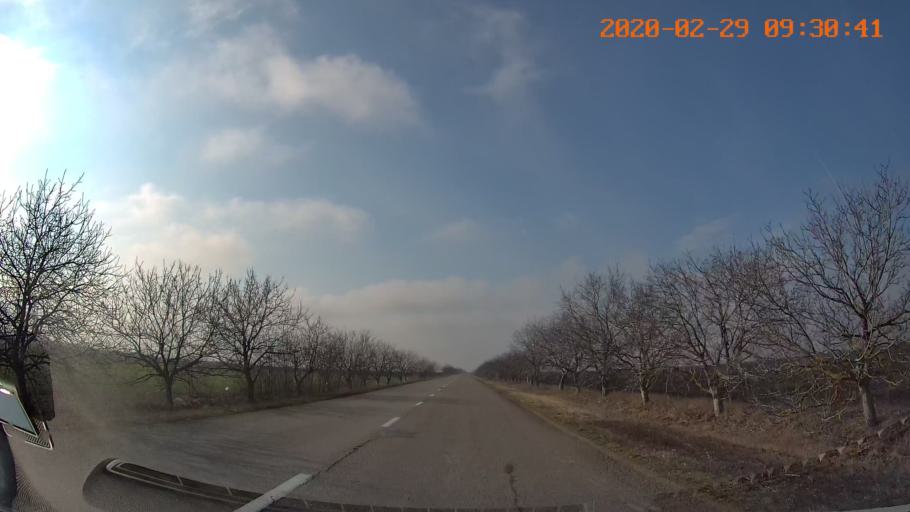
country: MD
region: Telenesti
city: Dnestrovsc
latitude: 46.6633
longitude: 29.9153
